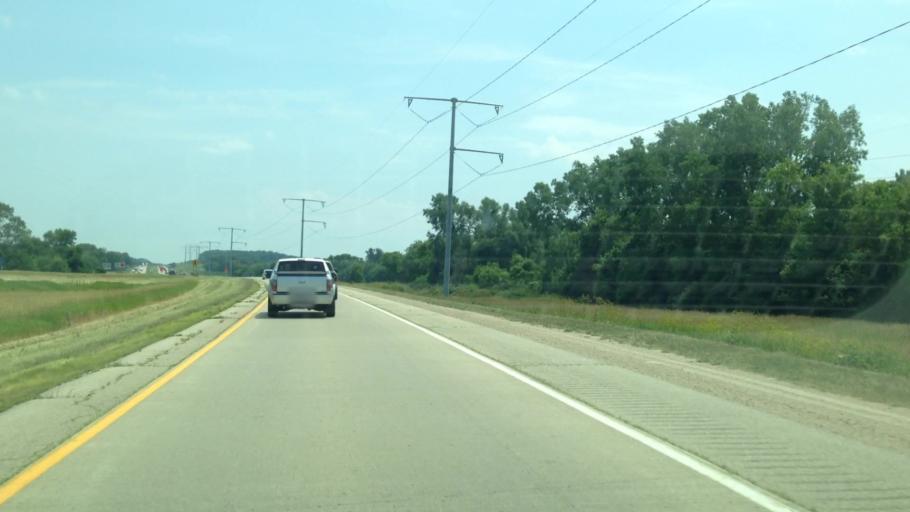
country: US
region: Wisconsin
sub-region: Dane County
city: McFarland
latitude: 43.0424
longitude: -89.2783
